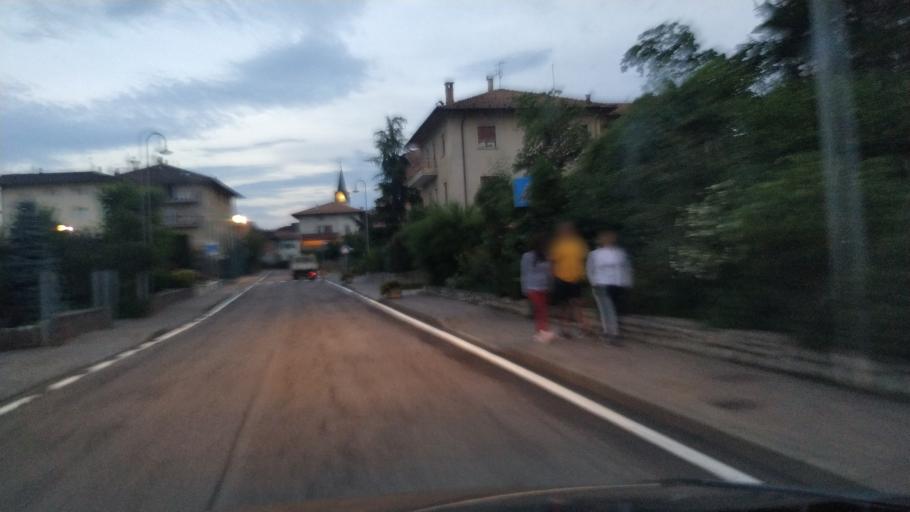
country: IT
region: Trentino-Alto Adige
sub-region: Provincia di Trento
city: Romallo
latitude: 46.3983
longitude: 11.0676
